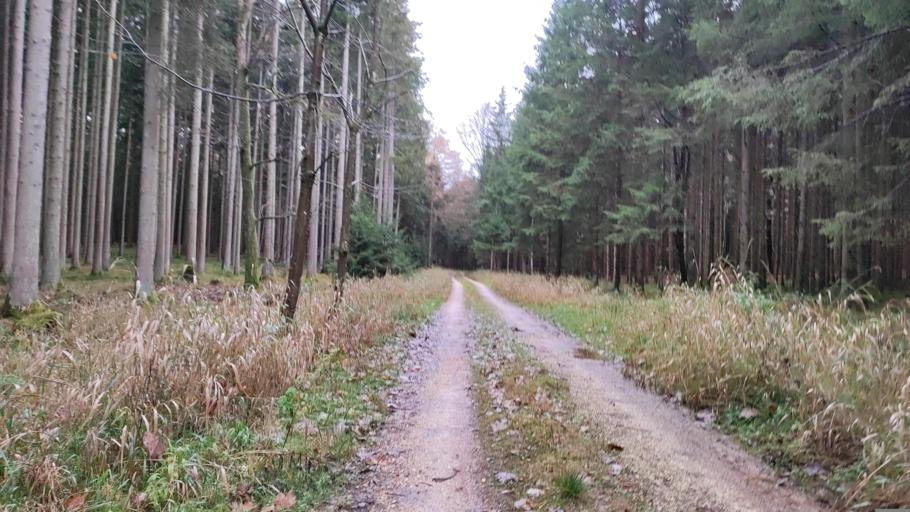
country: DE
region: Bavaria
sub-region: Swabia
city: Burtenbach
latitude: 48.3369
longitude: 10.5010
